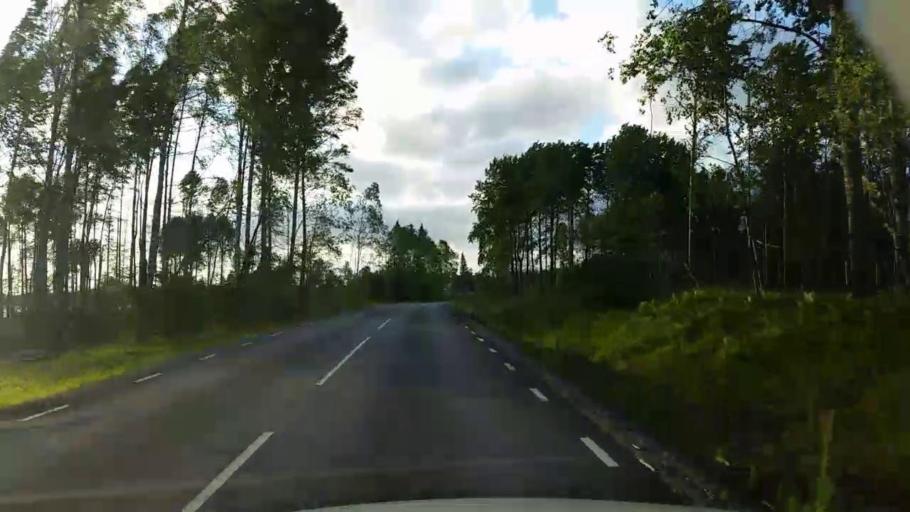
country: SE
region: Vaestmanland
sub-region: Kopings Kommun
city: Kolsva
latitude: 59.6625
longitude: 15.8356
